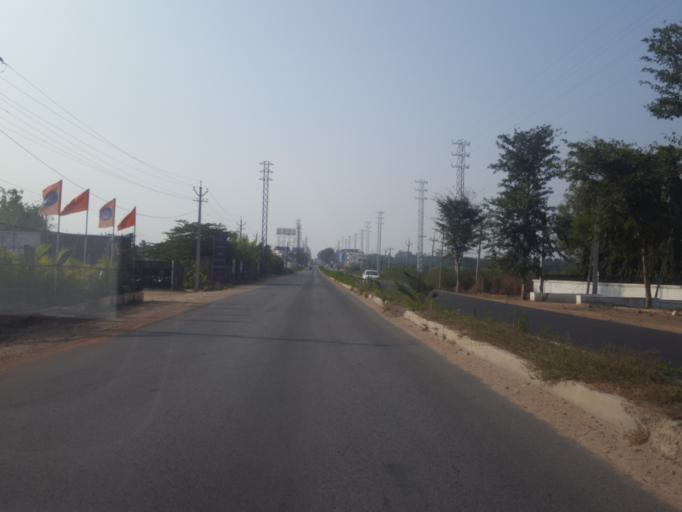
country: IN
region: Telangana
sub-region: Medak
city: Serilingampalle
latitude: 17.4026
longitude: 78.2905
